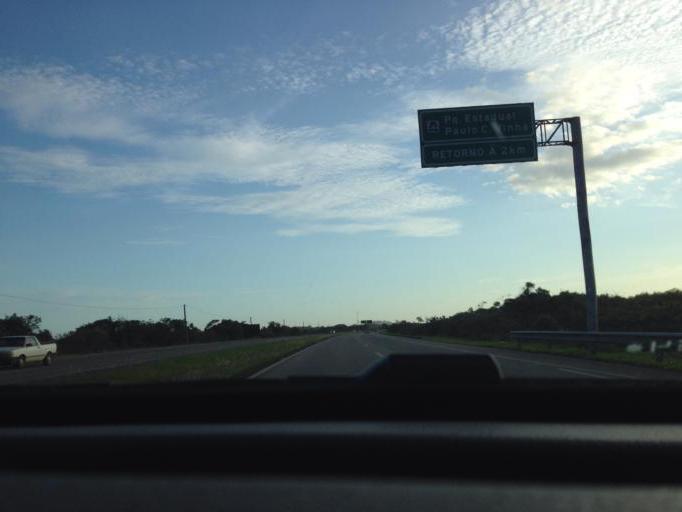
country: BR
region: Espirito Santo
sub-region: Guarapari
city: Guarapari
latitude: -20.6033
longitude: -40.4266
